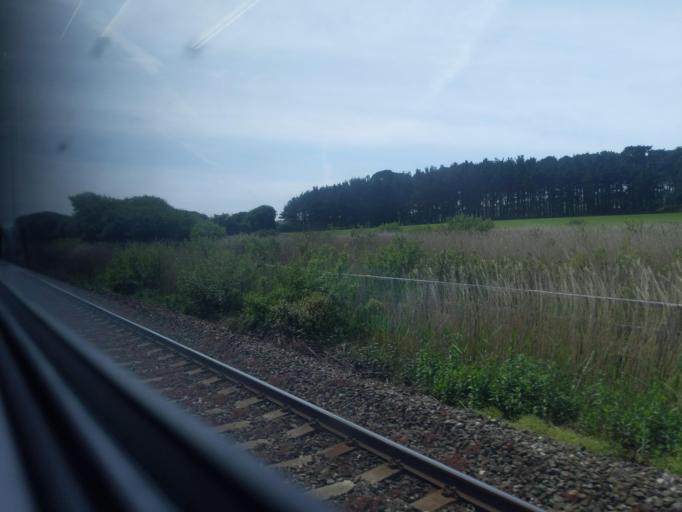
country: GB
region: England
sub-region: Cornwall
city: Marazion
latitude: 50.1316
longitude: -5.4836
